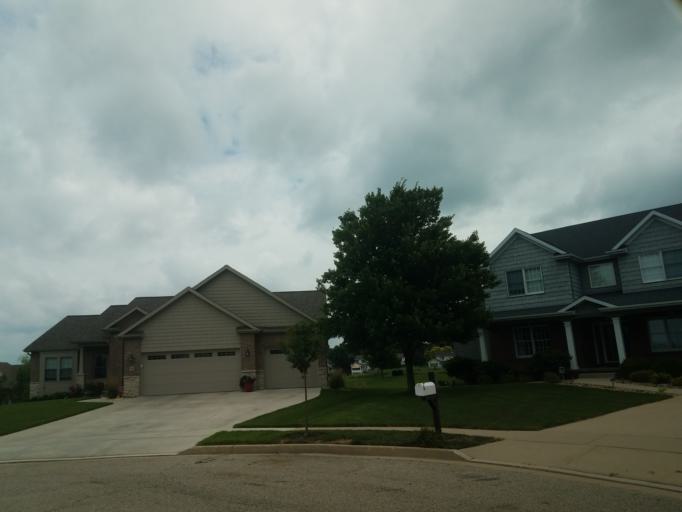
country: US
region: Illinois
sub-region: McLean County
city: Bloomington
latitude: 40.4483
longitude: -89.0374
